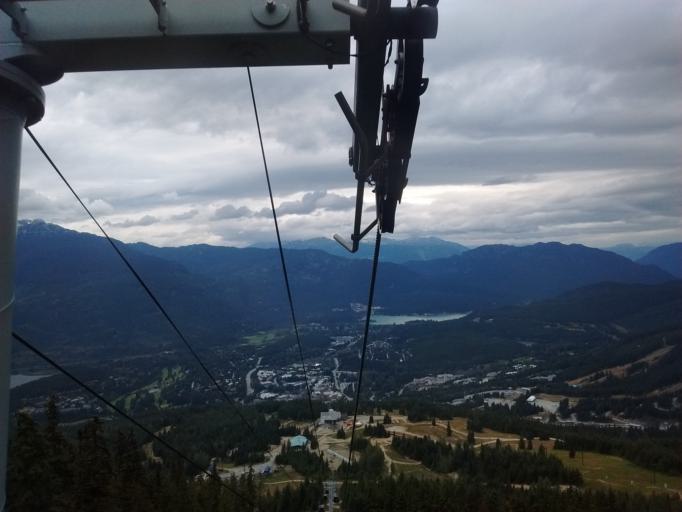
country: CA
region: British Columbia
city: Whistler
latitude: 50.0904
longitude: -122.9501
